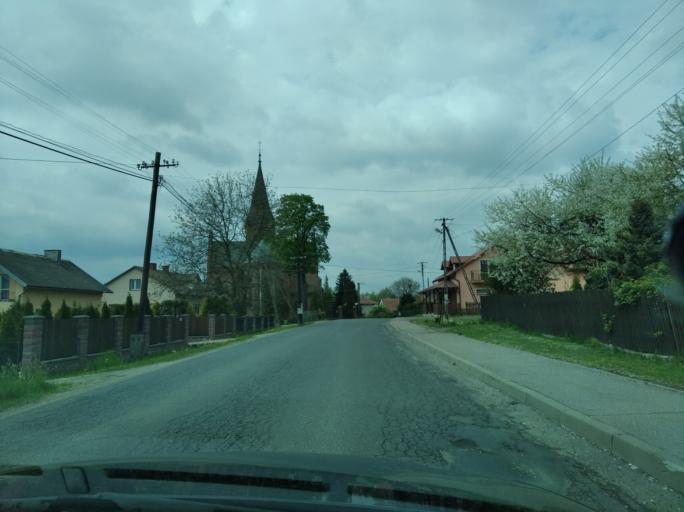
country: PL
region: Subcarpathian Voivodeship
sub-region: Powiat brzozowski
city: Jasionow
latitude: 49.6453
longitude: 21.9407
